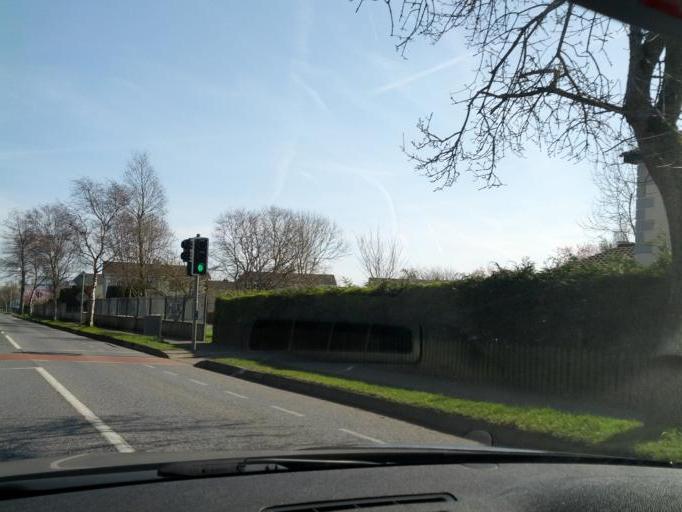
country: IE
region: Leinster
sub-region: Kildare
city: Celbridge
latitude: 53.3439
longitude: -6.5495
